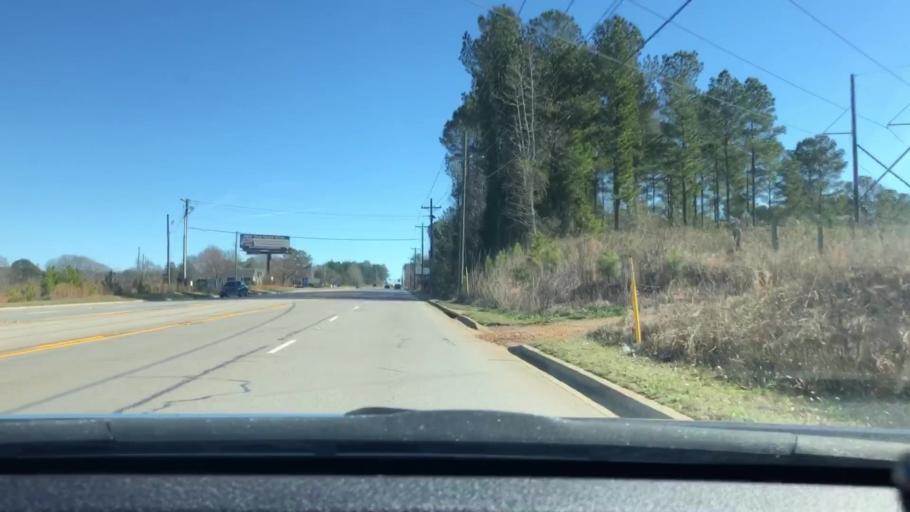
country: US
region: South Carolina
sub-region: Lexington County
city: Oak Grove
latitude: 34.0132
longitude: -81.1685
